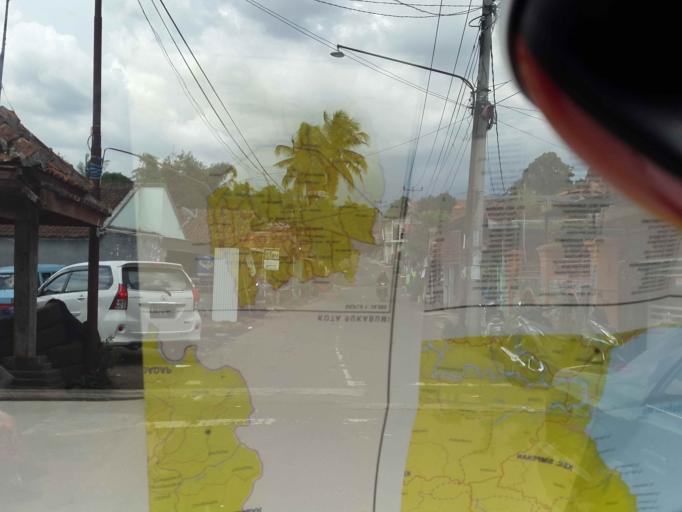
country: ID
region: West Java
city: Sukabumi
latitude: -6.9130
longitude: 106.9448
